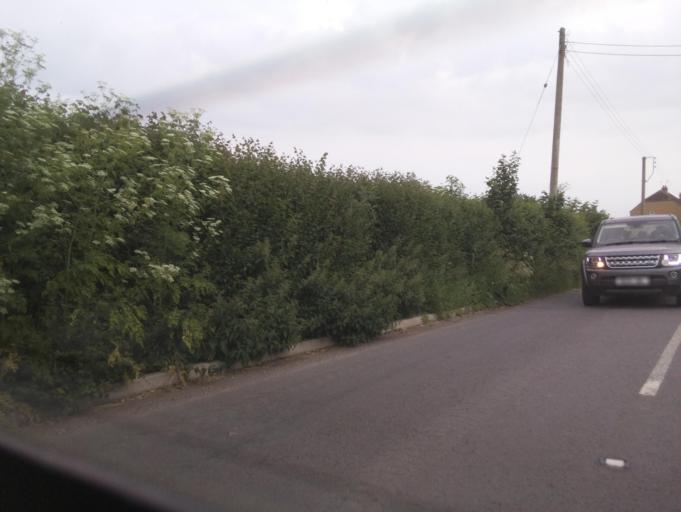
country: GB
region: England
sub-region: Somerset
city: Merriott
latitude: 50.9005
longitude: -2.7525
